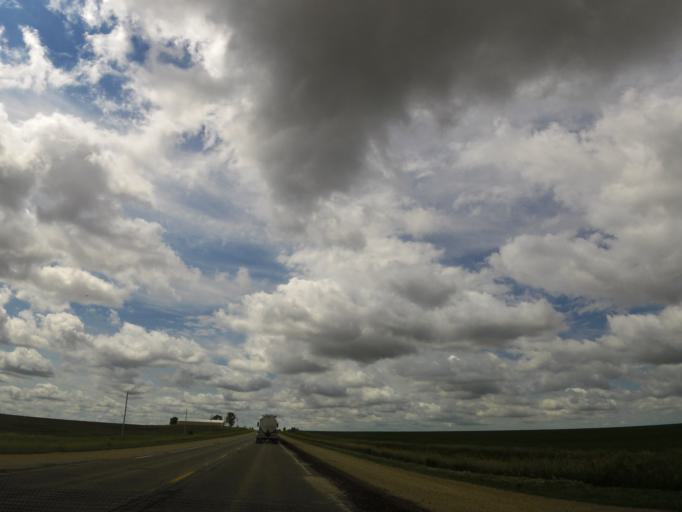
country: US
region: Iowa
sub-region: Howard County
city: Cresco
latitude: 43.3278
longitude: -92.2989
